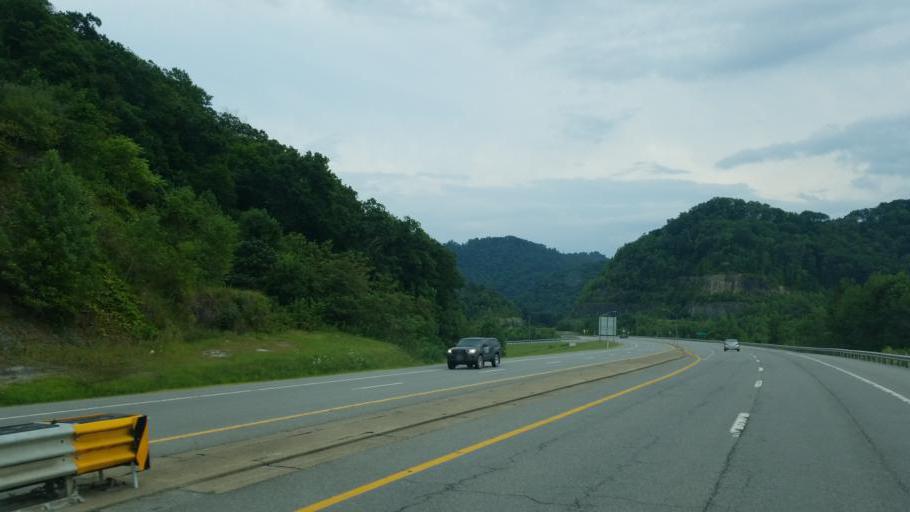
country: US
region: West Virginia
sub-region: Logan County
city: Mount Gay-Shamrock
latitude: 37.8391
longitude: -82.0476
